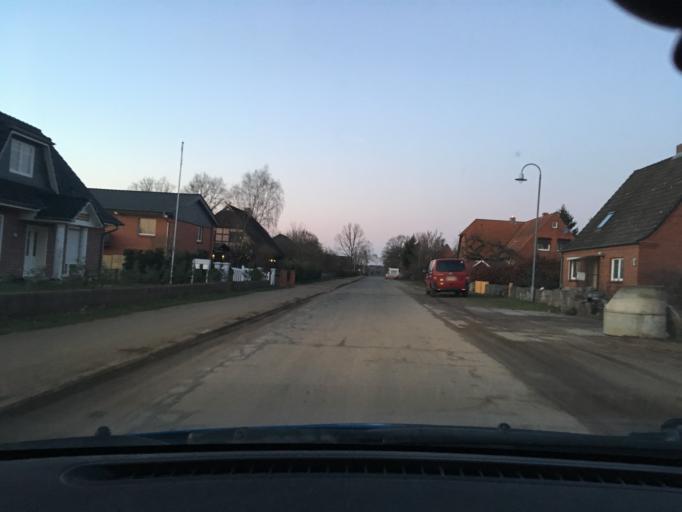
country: DE
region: Schleswig-Holstein
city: Fitzen
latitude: 53.4979
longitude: 10.6482
